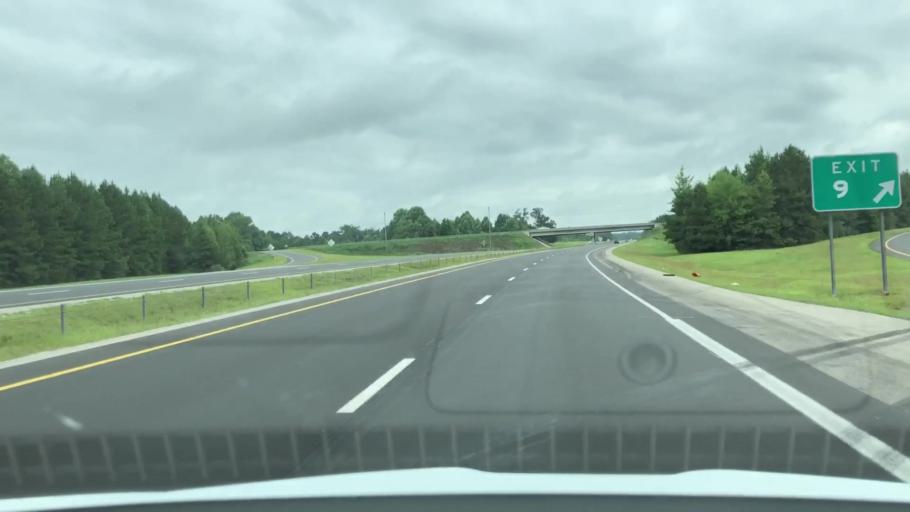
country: US
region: North Carolina
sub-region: Wilson County
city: Lucama
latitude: 35.6169
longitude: -77.9789
